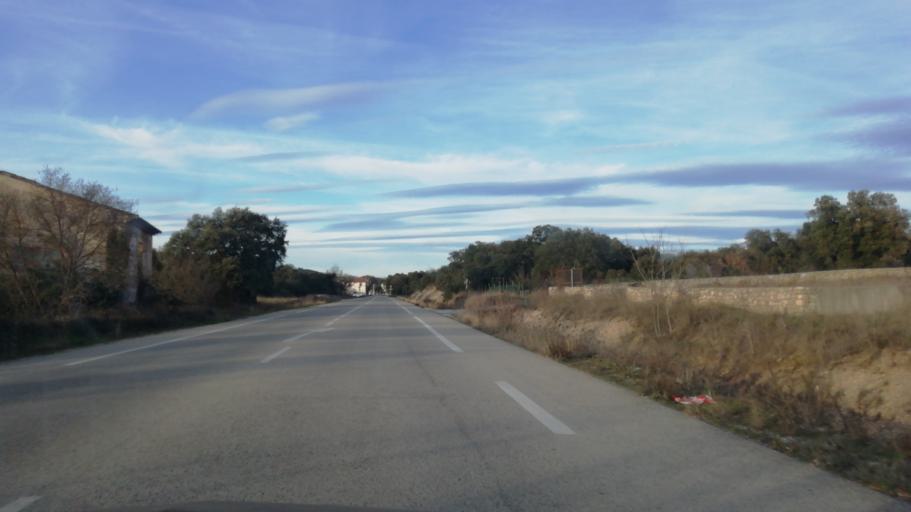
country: FR
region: Languedoc-Roussillon
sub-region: Departement du Gard
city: Quissac
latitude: 43.8999
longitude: 4.0068
